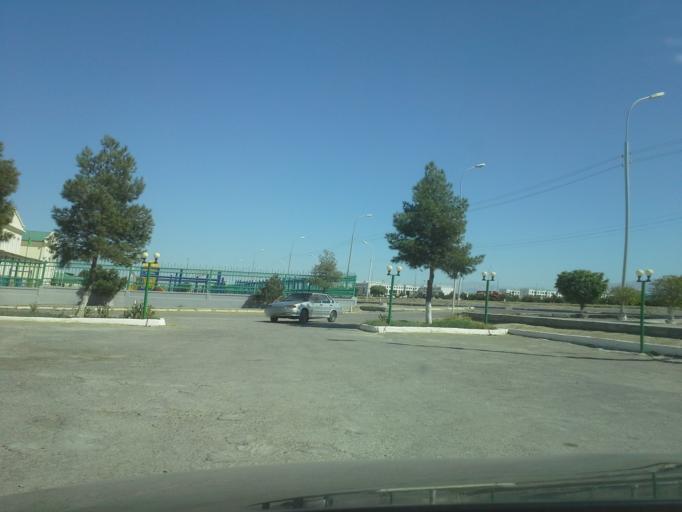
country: TM
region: Ahal
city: Abadan
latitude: 38.0491
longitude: 58.1970
